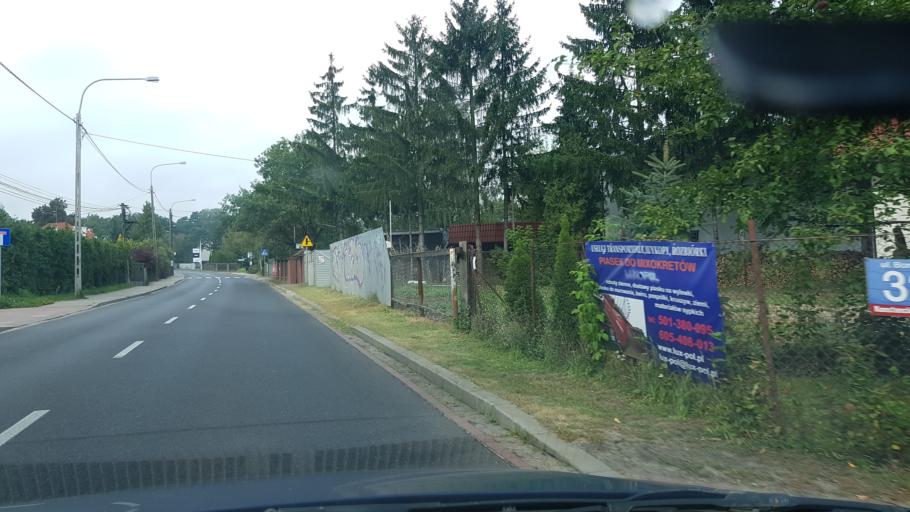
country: PL
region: Masovian Voivodeship
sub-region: Powiat piaseczynski
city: Konstancin-Jeziorna
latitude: 52.1057
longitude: 21.1077
